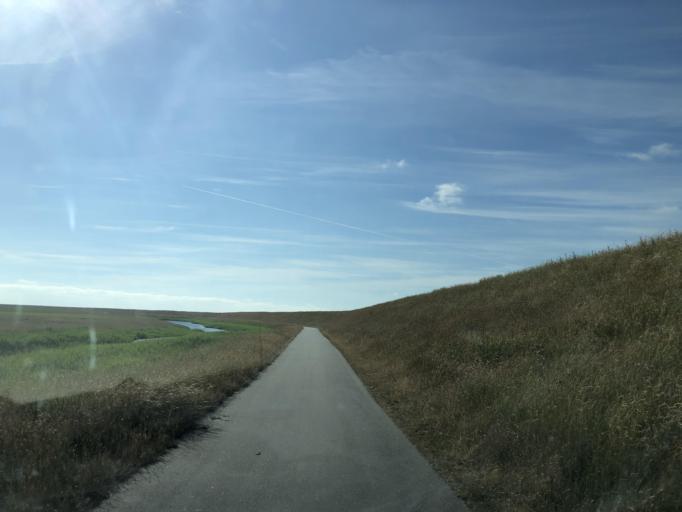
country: DK
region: South Denmark
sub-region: Esbjerg Kommune
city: Tjaereborg
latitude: 55.2933
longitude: 8.5643
